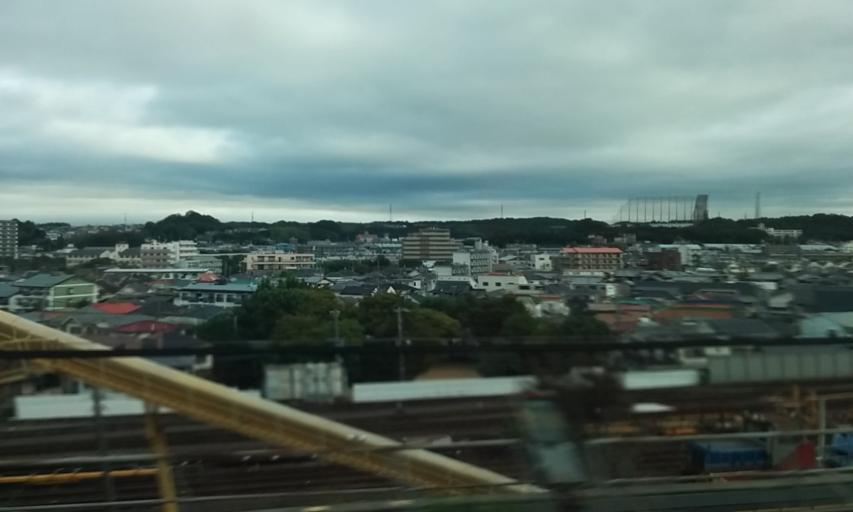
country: JP
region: Hyogo
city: Akashi
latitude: 34.6677
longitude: 135.0147
